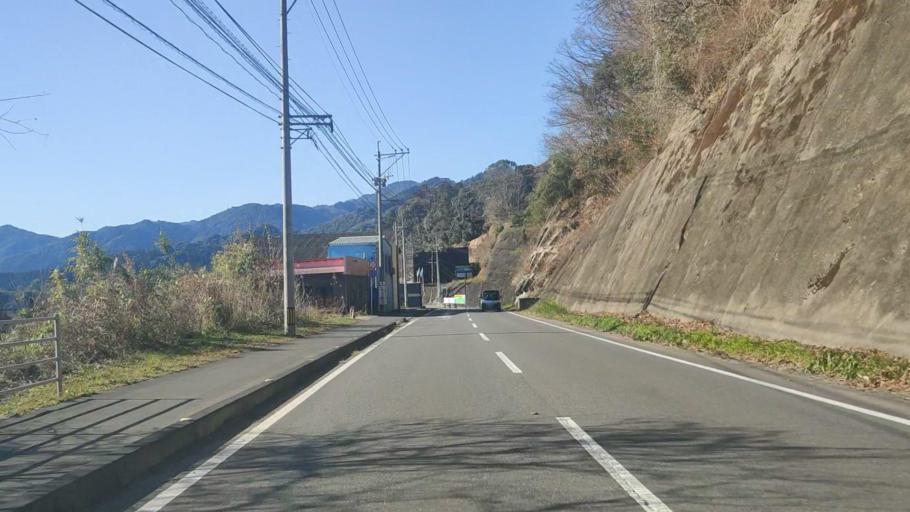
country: JP
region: Oita
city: Saiki
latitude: 32.9758
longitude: 131.8550
